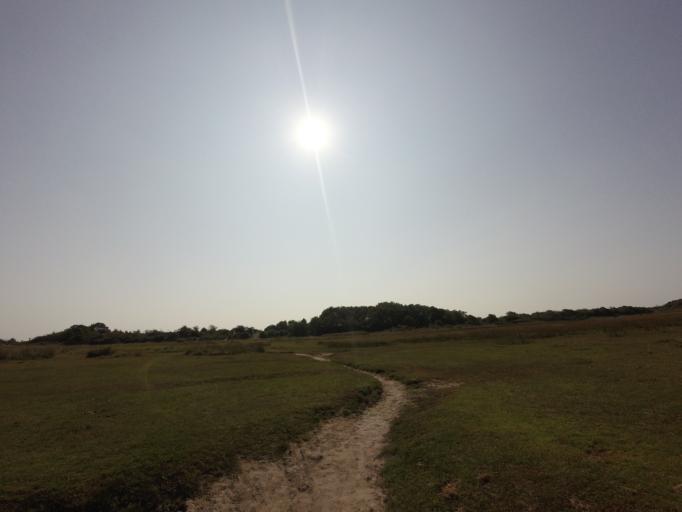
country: NL
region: Friesland
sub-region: Gemeente Schiermonnikoog
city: Schiermonnikoog
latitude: 53.4887
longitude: 6.2234
